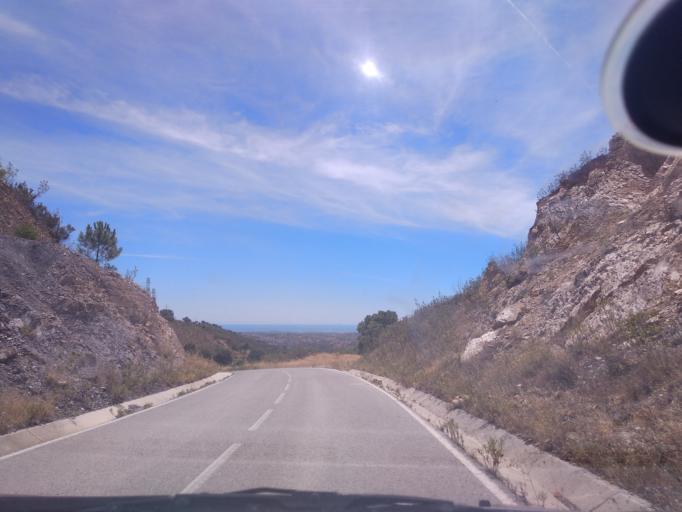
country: PT
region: Faro
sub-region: Sao Bras de Alportel
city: Sao Bras de Alportel
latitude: 37.1985
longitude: -7.8056
